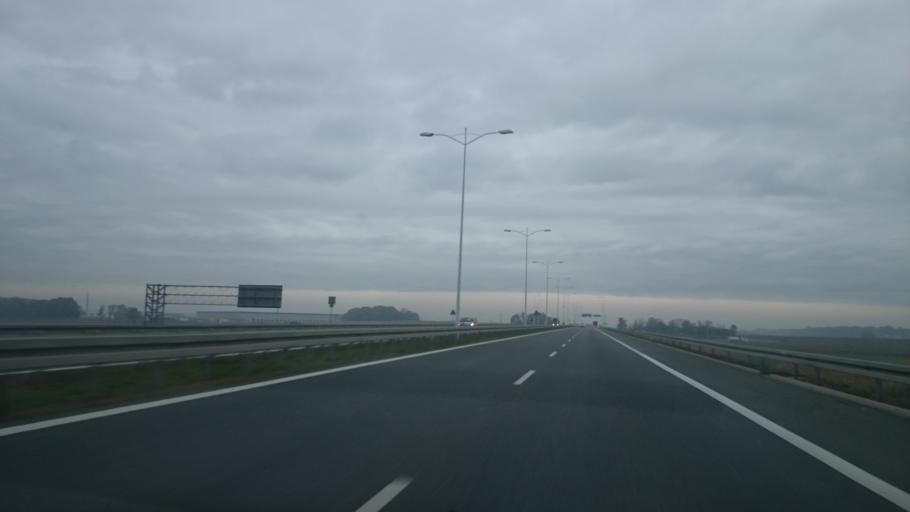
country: PL
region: Lower Silesian Voivodeship
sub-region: Powiat wroclawski
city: Tyniec Maly
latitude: 51.0253
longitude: 16.9413
